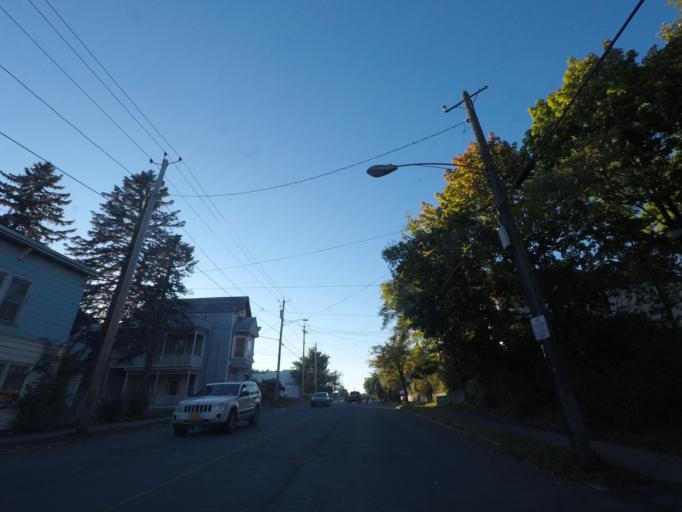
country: US
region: New York
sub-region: Albany County
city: Cohoes
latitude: 42.7726
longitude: -73.6858
